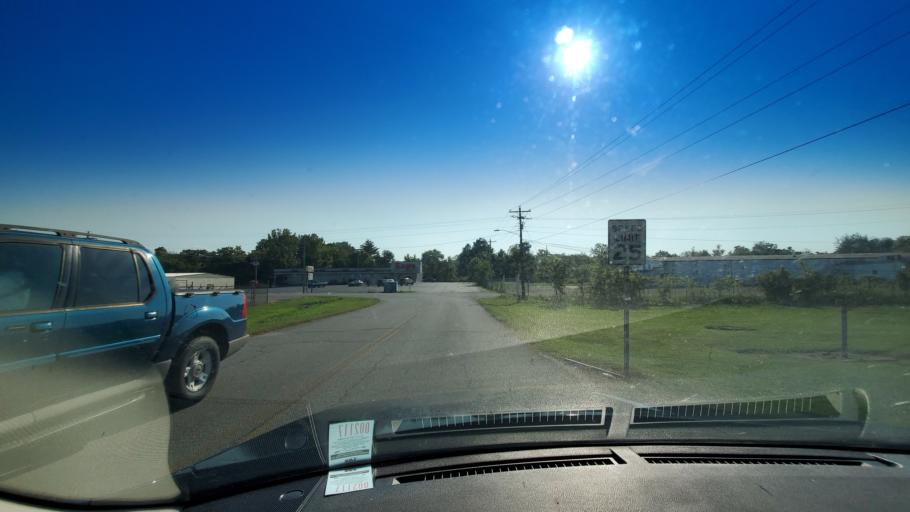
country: US
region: Tennessee
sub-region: Smith County
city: Carthage
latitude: 36.2636
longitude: -85.9575
